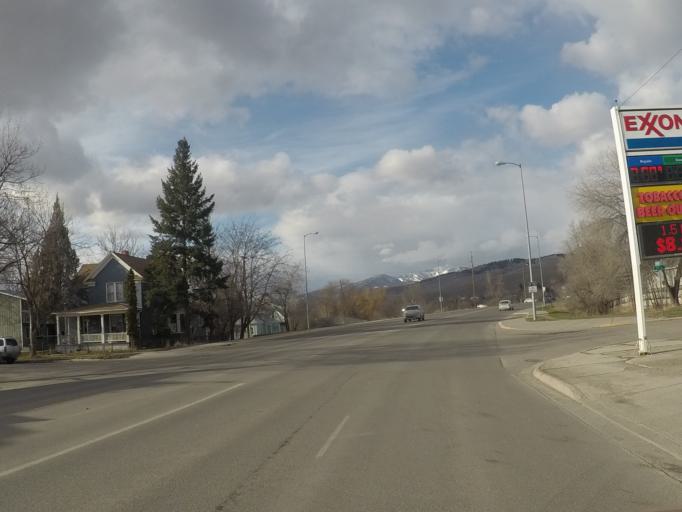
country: US
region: Montana
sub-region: Missoula County
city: Missoula
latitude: 46.8687
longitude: -114.0035
